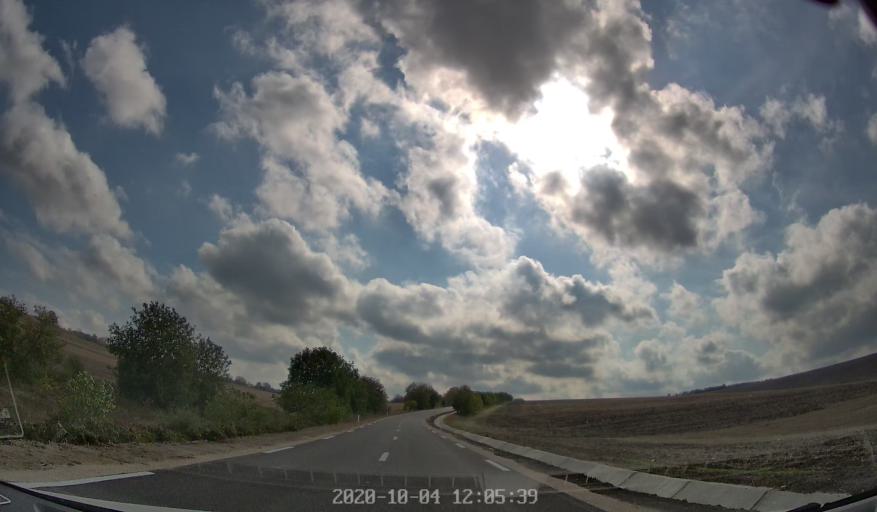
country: MD
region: Rezina
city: Saharna
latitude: 47.5921
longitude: 28.9520
